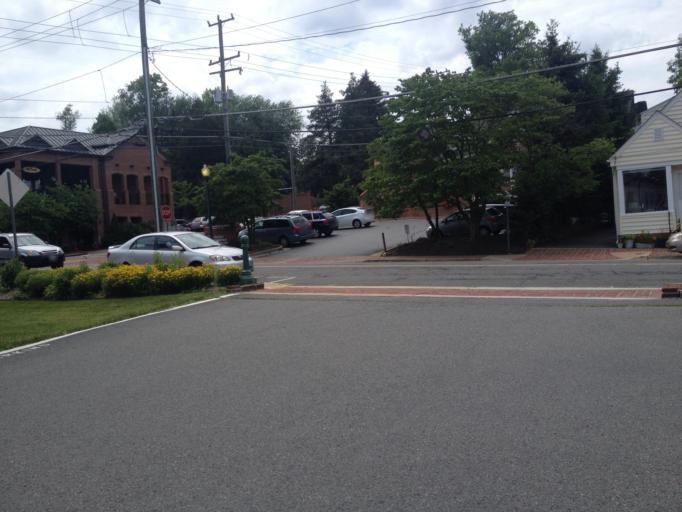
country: US
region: Virginia
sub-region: Fairfax County
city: Vienna
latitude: 38.9027
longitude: -77.2659
